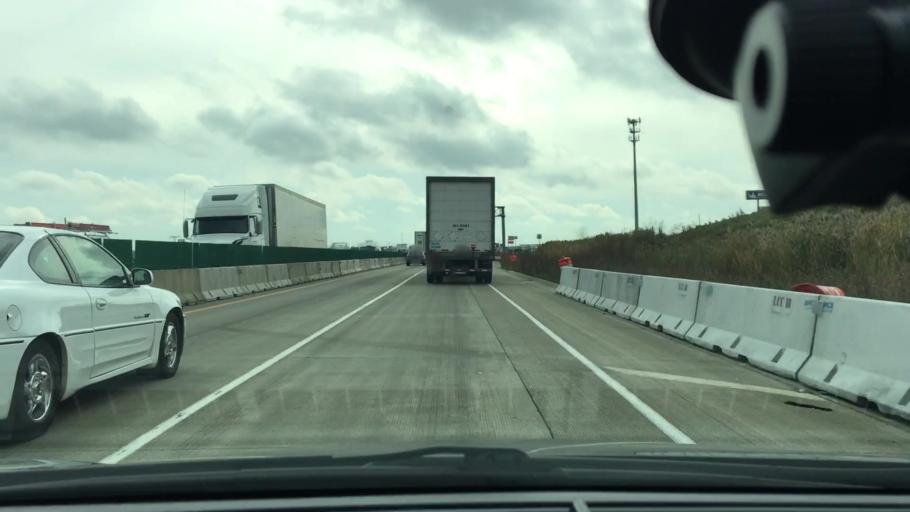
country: US
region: Wisconsin
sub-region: Racine County
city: Franksville
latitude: 42.7330
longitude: -87.9542
